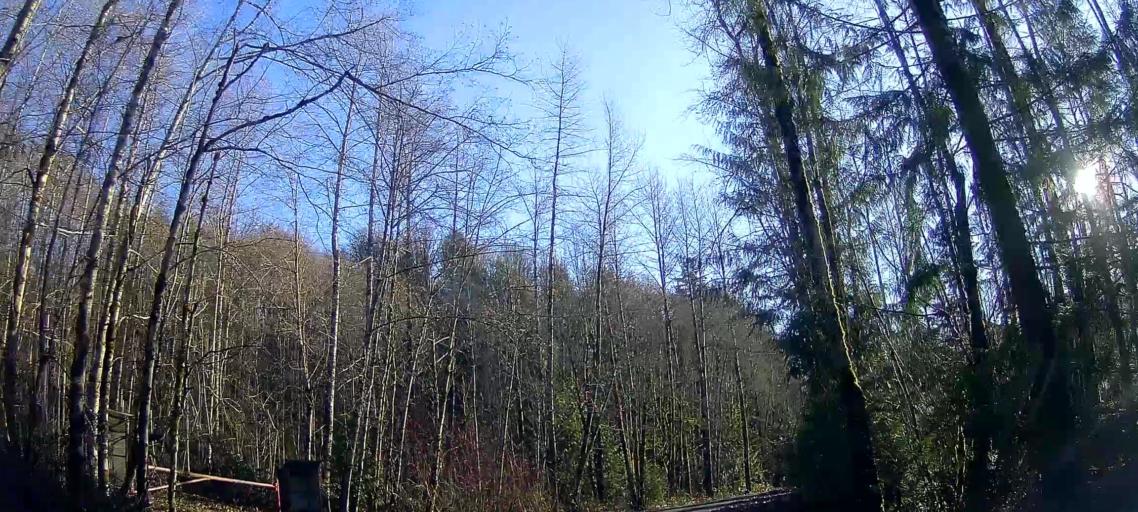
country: US
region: Washington
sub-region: Snohomish County
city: Darrington
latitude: 48.5449
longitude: -121.7378
